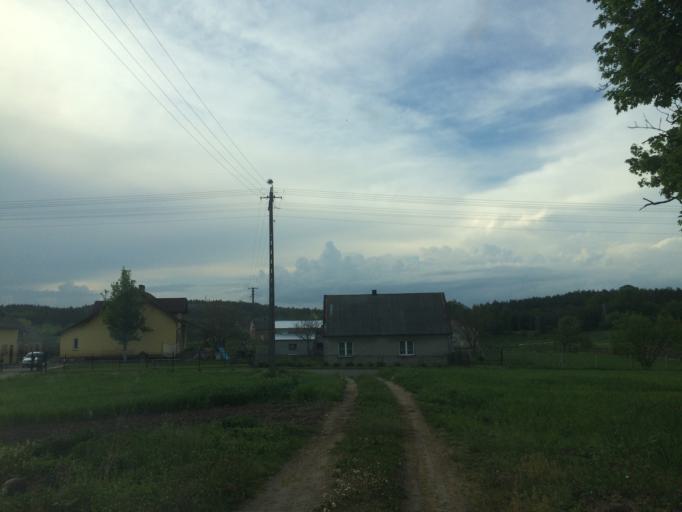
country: PL
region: Warmian-Masurian Voivodeship
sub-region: Powiat ilawski
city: Lubawa
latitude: 53.4309
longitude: 19.6939
